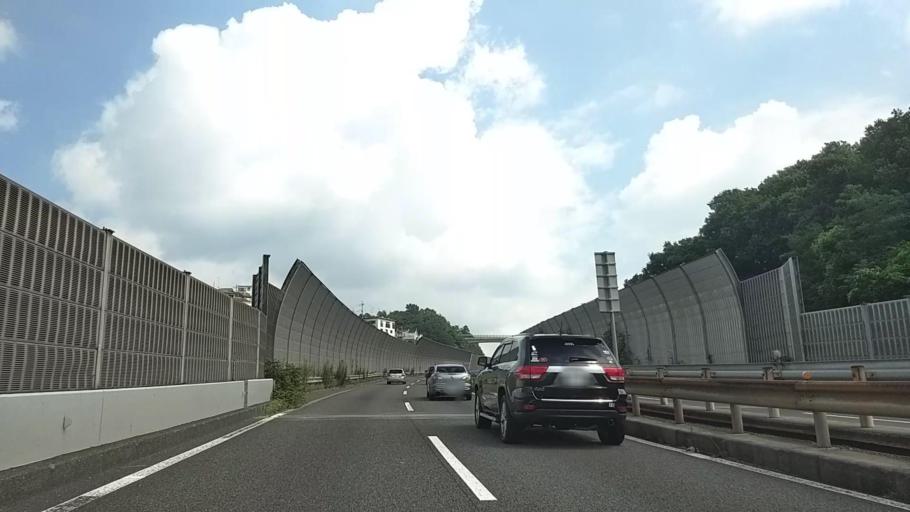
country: JP
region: Tokyo
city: Hachioji
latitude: 35.6067
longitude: 139.3383
